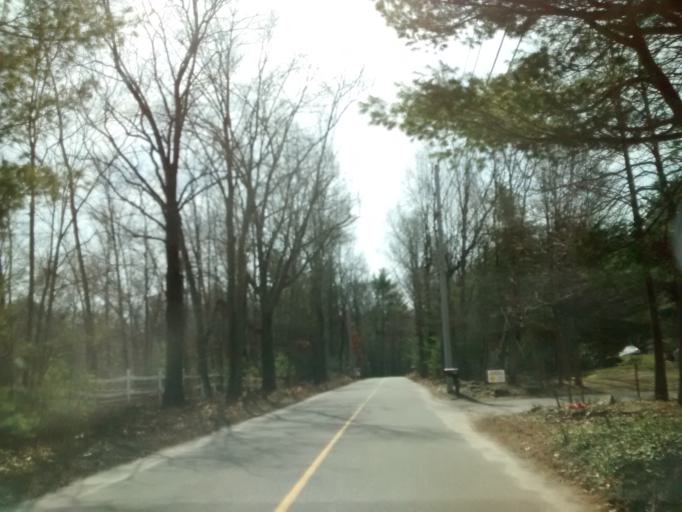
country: US
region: Massachusetts
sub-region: Worcester County
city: Southbridge
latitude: 42.1140
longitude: -72.0221
